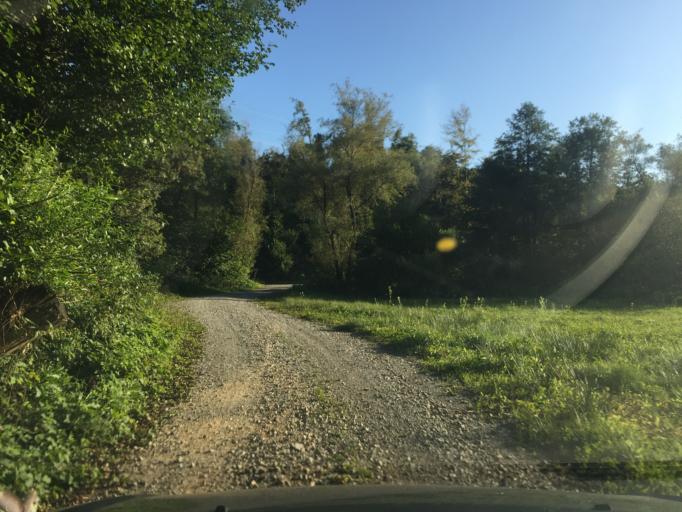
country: SI
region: Postojna
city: Postojna
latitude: 45.8076
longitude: 14.1337
